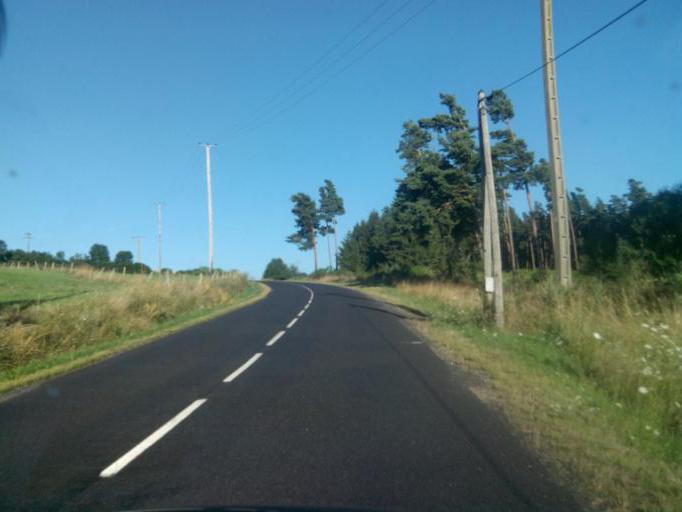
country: FR
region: Rhone-Alpes
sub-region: Departement de la Loire
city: Usson-en-Forez
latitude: 45.3546
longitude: 3.9059
